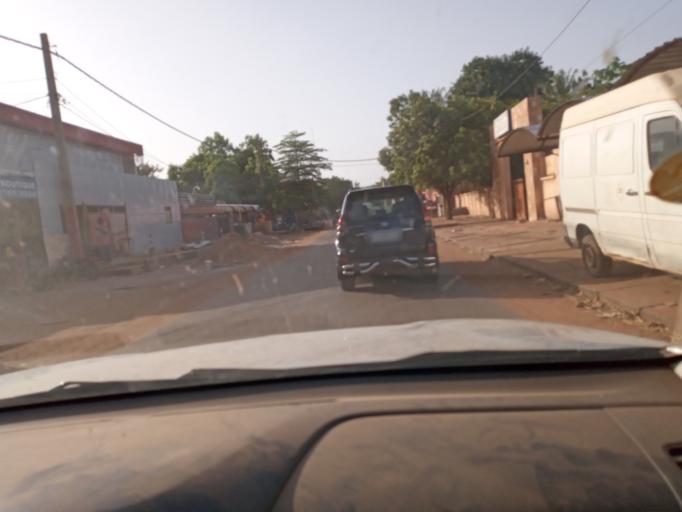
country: ML
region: Bamako
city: Bamako
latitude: 12.6587
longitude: -7.9716
